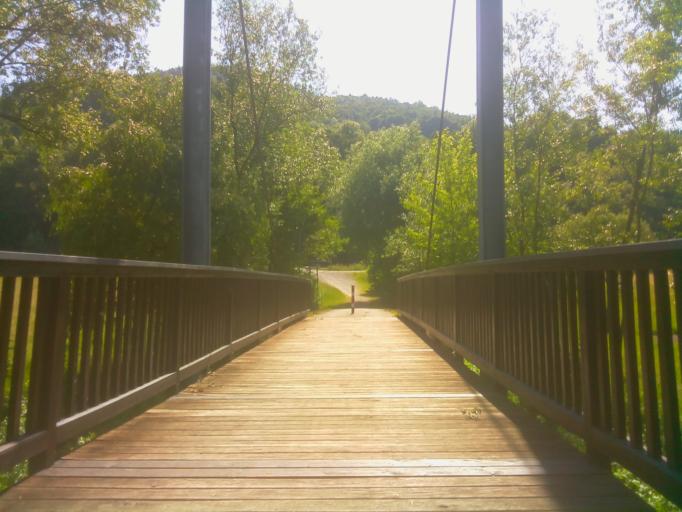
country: DE
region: Thuringia
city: Rudolstadt
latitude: 50.6904
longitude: 11.3362
